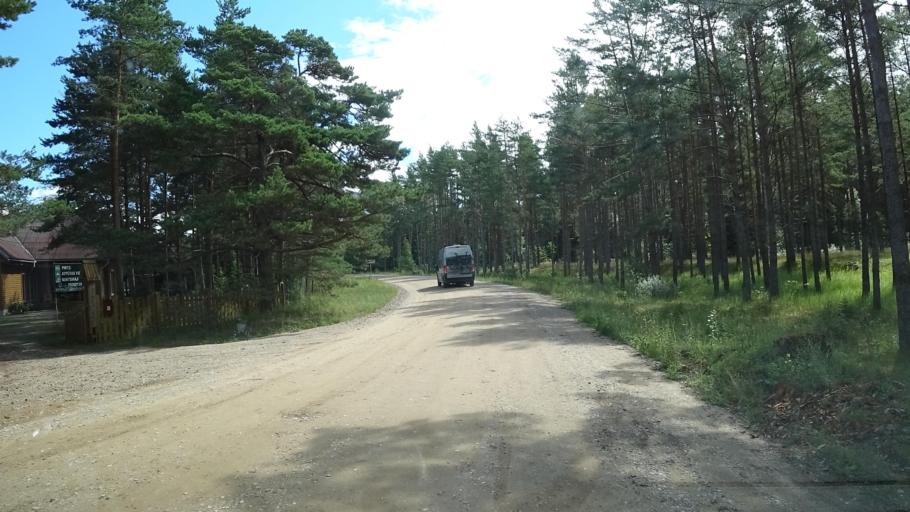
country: LV
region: Ventspils
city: Ventspils
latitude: 57.4870
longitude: 21.6490
